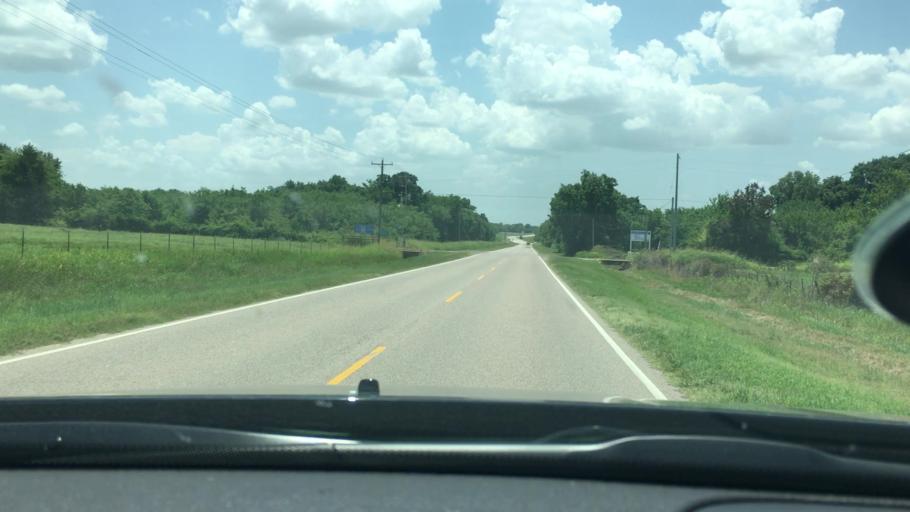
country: US
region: Oklahoma
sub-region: Johnston County
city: Tishomingo
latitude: 34.4641
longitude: -96.6360
